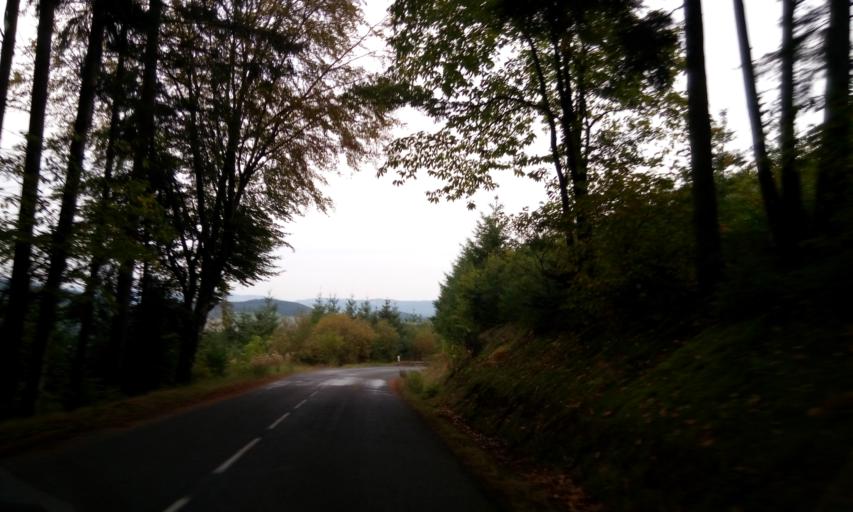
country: FR
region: Rhone-Alpes
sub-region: Departement du Rhone
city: Cublize
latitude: 45.9966
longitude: 4.4274
